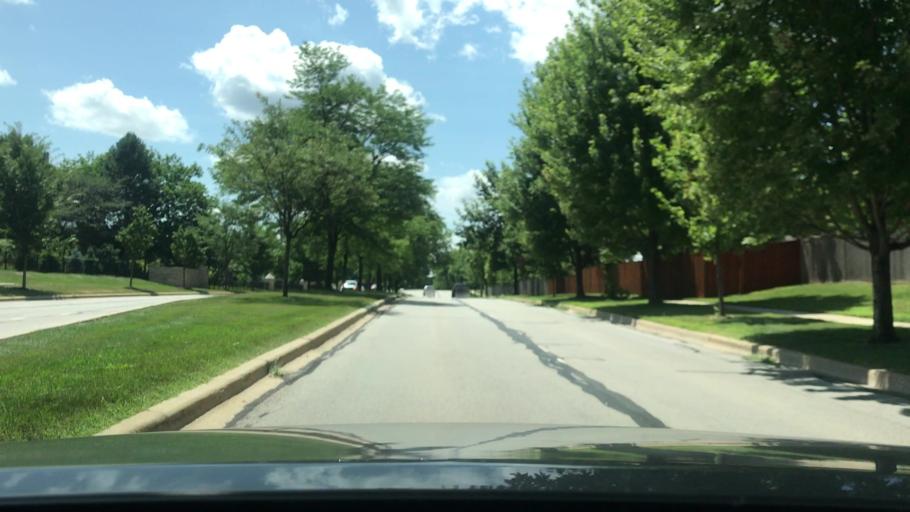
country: US
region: Illinois
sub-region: DuPage County
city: Naperville
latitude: 41.7626
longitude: -88.1132
